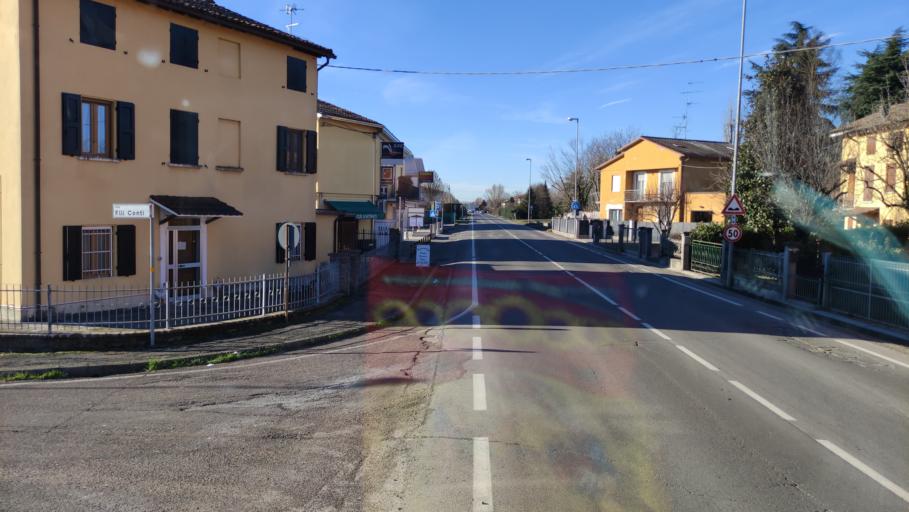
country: IT
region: Emilia-Romagna
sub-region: Provincia di Reggio Emilia
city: Campagnola Emilia
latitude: 44.8329
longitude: 10.7782
